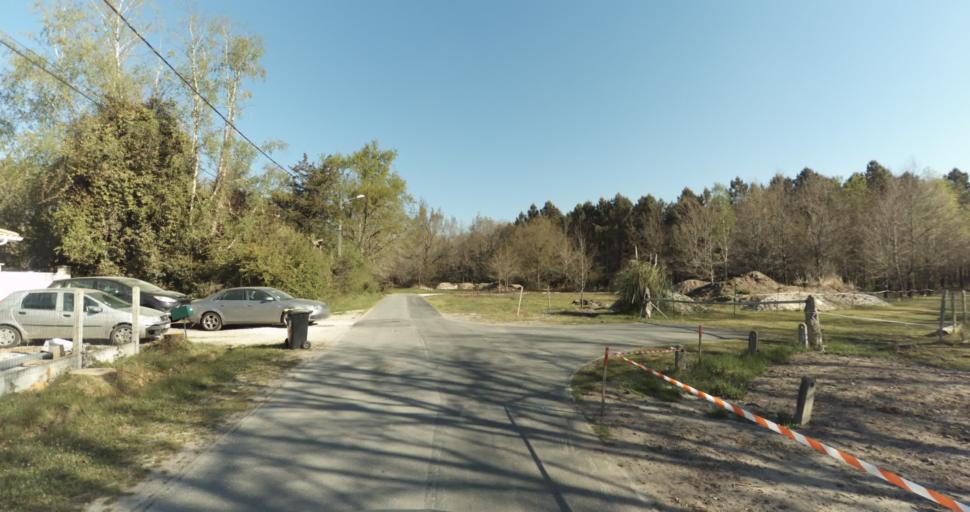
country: FR
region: Aquitaine
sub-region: Departement de la Gironde
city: Martignas-sur-Jalle
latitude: 44.8081
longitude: -0.8442
